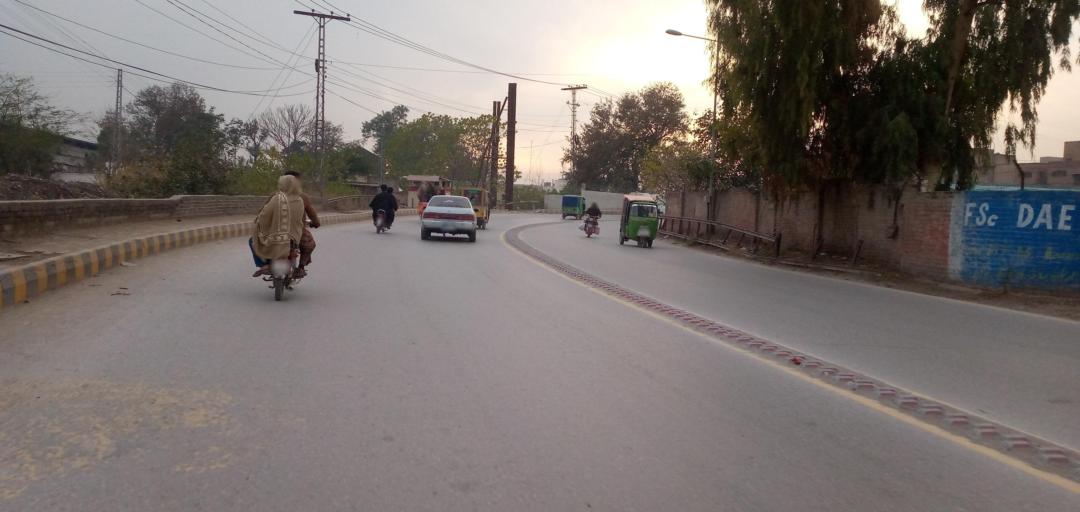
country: PK
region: Khyber Pakhtunkhwa
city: Peshawar
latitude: 33.9996
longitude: 71.5486
